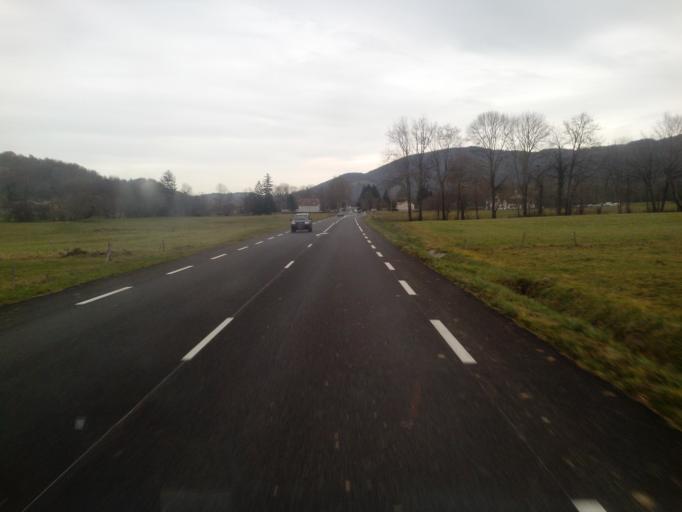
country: FR
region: Midi-Pyrenees
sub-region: Departement de l'Ariege
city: Foix
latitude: 43.0092
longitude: 1.4567
